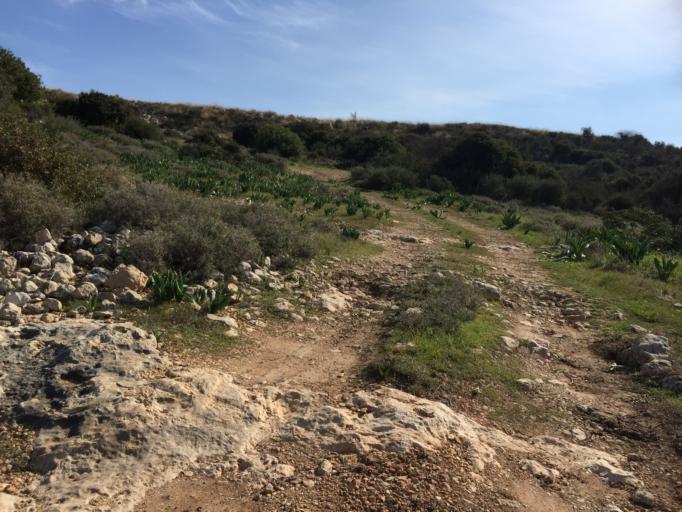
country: CY
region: Larnaka
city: Agios Tychon
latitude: 34.7444
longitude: 33.1181
